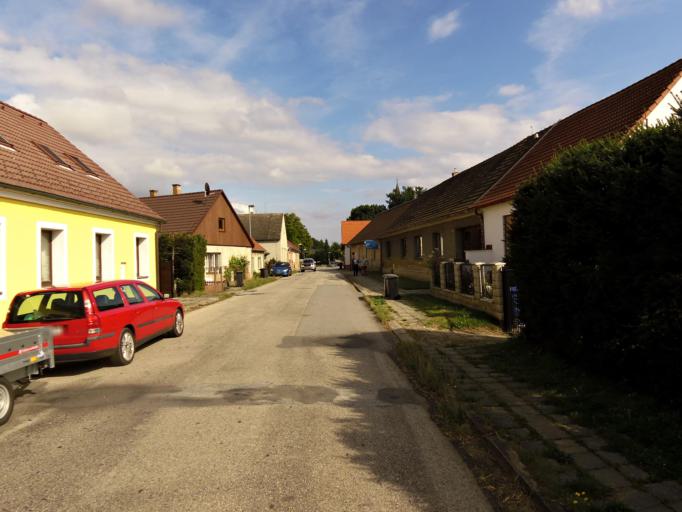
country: CZ
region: Jihocesky
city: Suchdol nad Luznici
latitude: 48.8886
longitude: 14.8728
